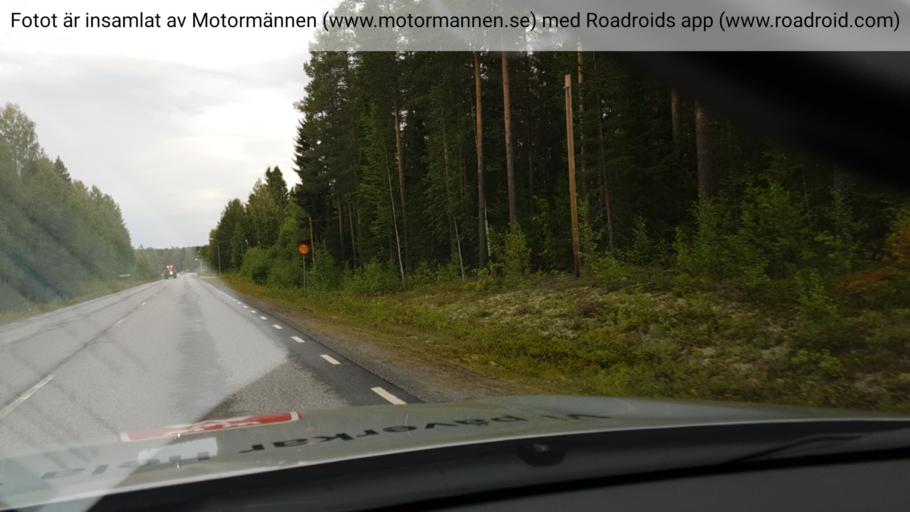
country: SE
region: Norrbotten
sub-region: Bodens Kommun
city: Boden
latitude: 65.8102
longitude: 21.6527
